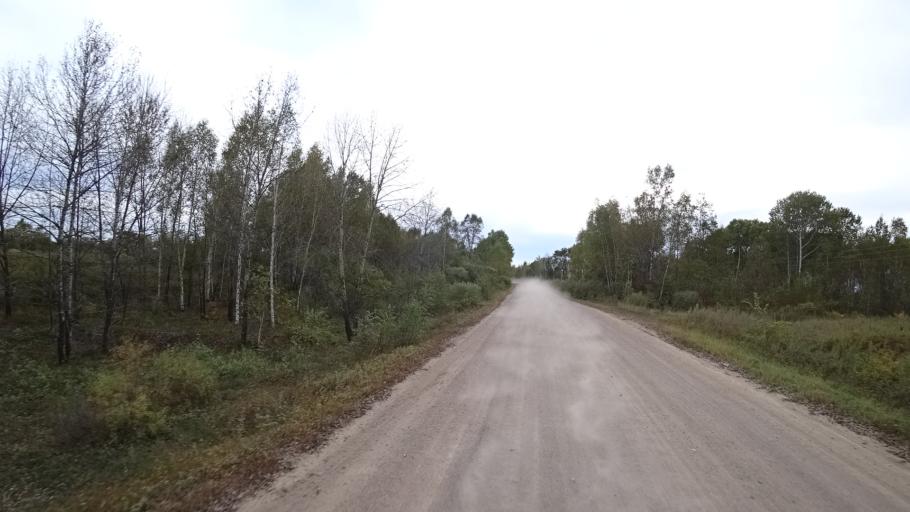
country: RU
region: Amur
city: Arkhara
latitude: 49.3829
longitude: 130.2198
